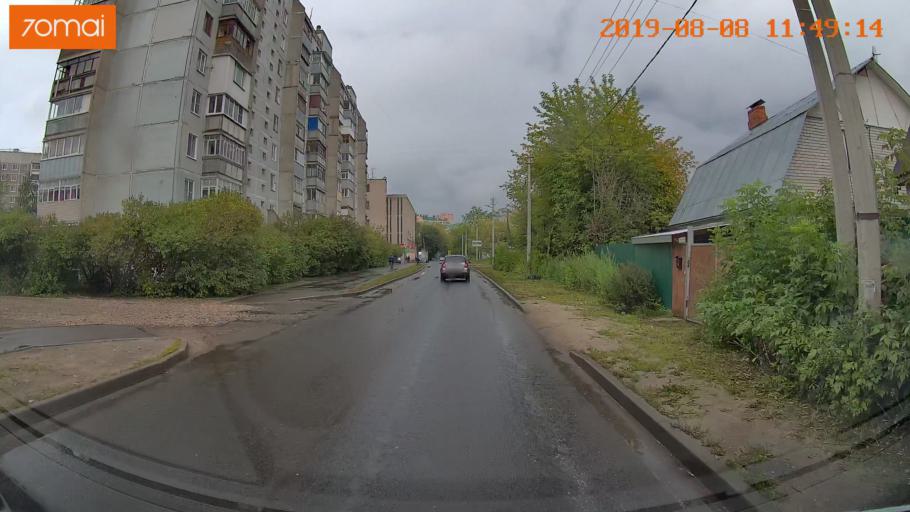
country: RU
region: Ivanovo
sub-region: Gorod Ivanovo
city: Ivanovo
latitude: 56.9767
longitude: 40.9822
